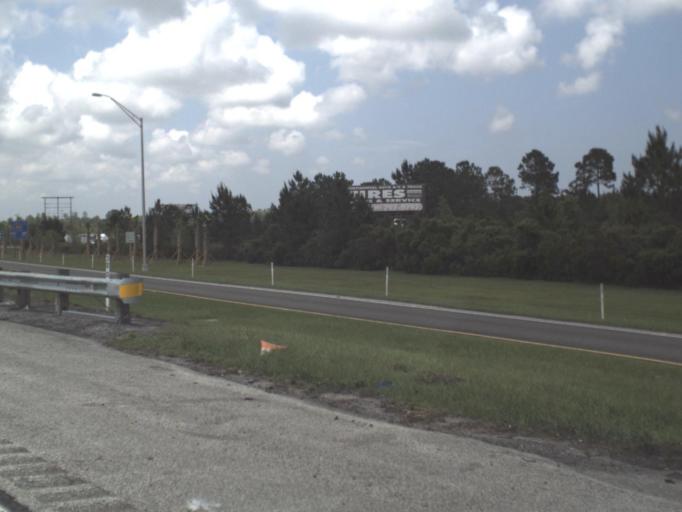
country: US
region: Florida
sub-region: Saint Johns County
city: Saint Augustine Shores
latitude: 29.7453
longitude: -81.3453
